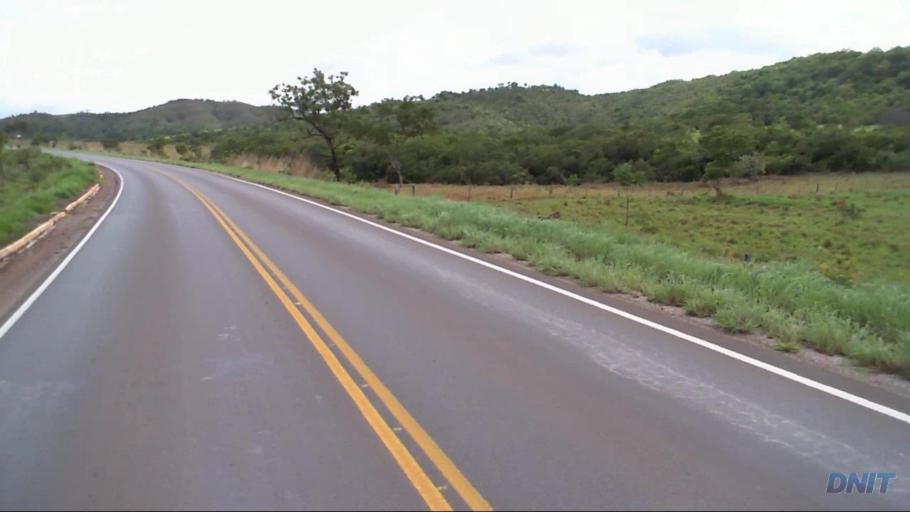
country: BR
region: Goias
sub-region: Padre Bernardo
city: Padre Bernardo
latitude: -15.4367
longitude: -48.1931
